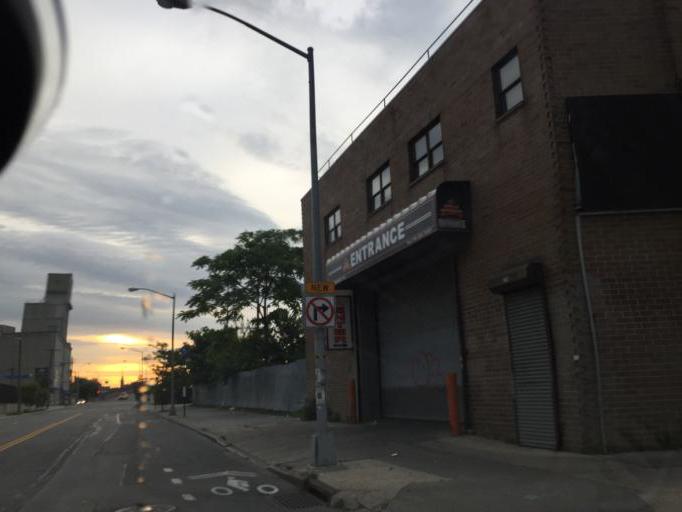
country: US
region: New York
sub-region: Queens County
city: Long Island City
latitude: 40.7320
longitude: -73.9447
